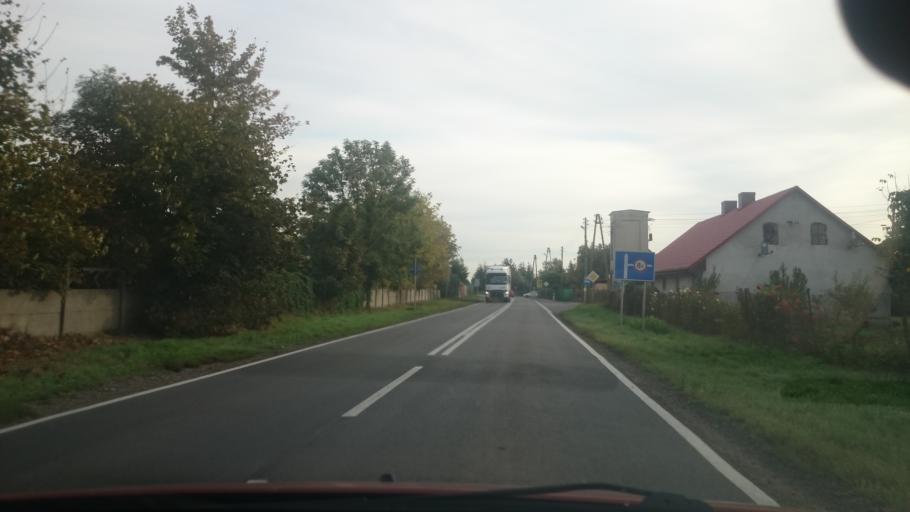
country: PL
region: Lower Silesian Voivodeship
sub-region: Powiat trzebnicki
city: Trzebnica
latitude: 51.3473
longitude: 17.1105
